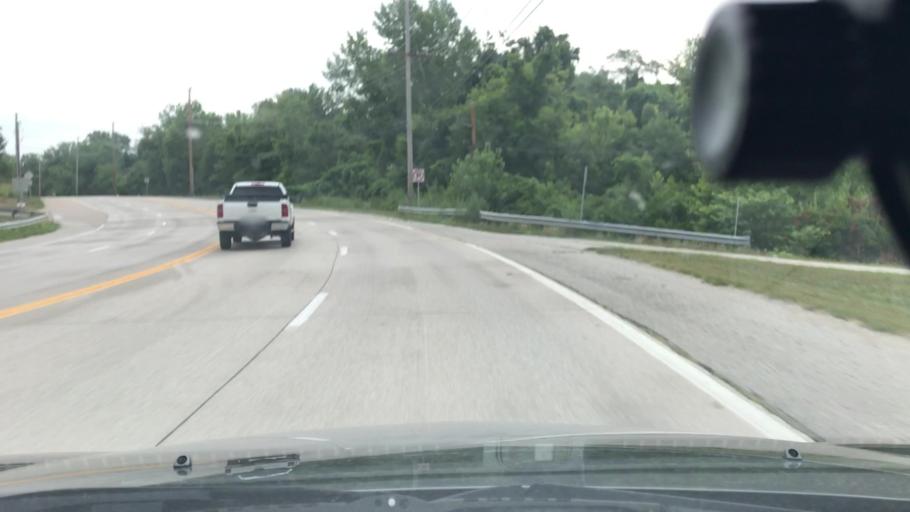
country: US
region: Missouri
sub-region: Saint Charles County
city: Saint Charles
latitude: 38.7430
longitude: -90.5185
